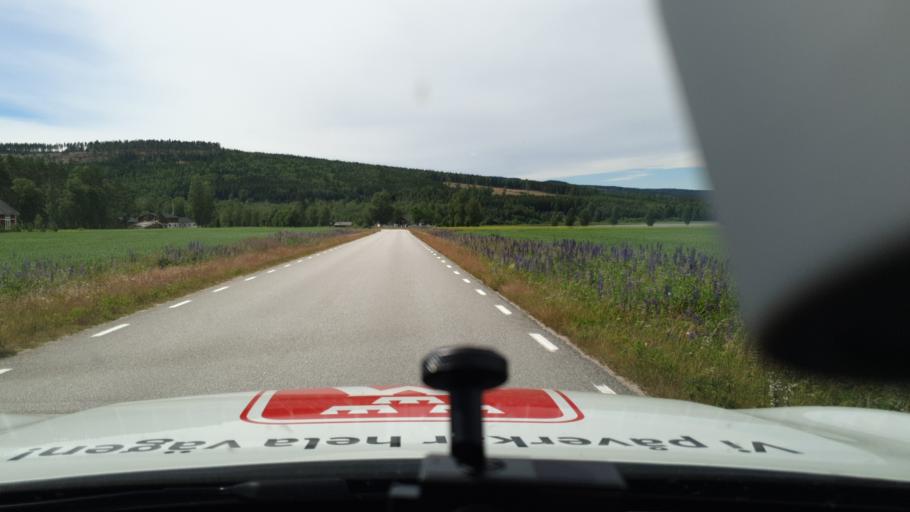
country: SE
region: Vaermland
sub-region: Hagfors Kommun
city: Ekshaerad
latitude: 60.0713
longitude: 13.4916
